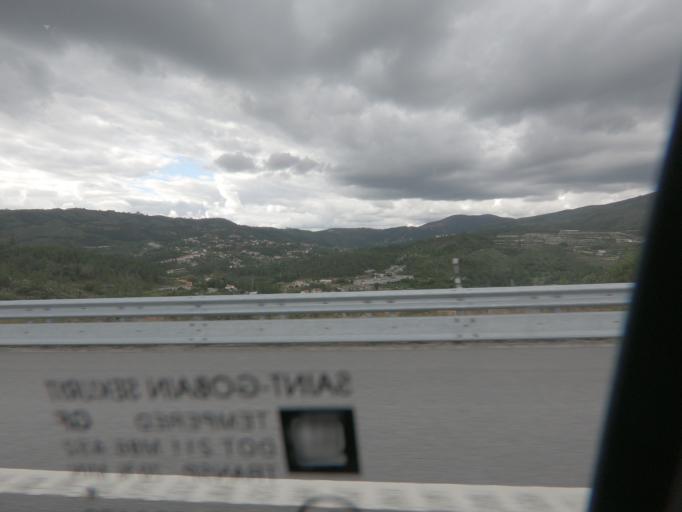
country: PT
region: Porto
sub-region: Amarante
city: Amarante
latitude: 41.2596
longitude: -8.0040
